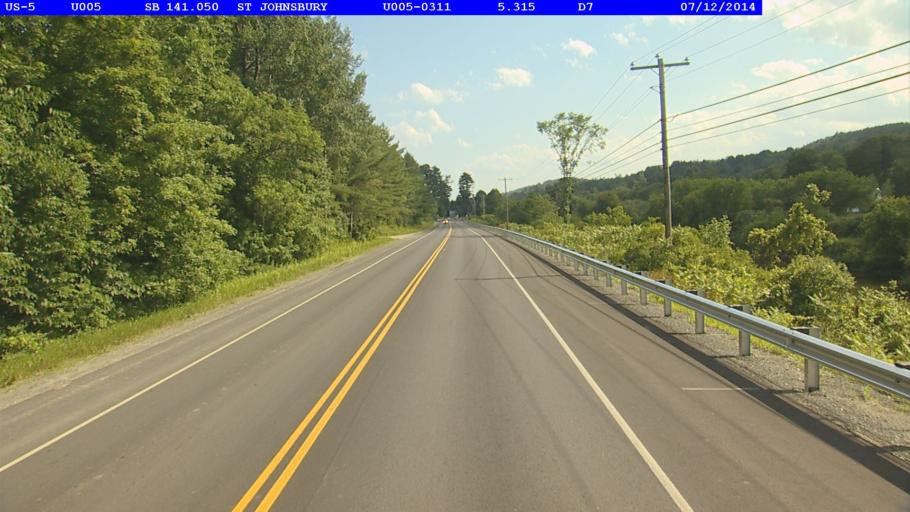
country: US
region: Vermont
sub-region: Caledonia County
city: St Johnsbury
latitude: 44.4675
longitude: -72.0135
